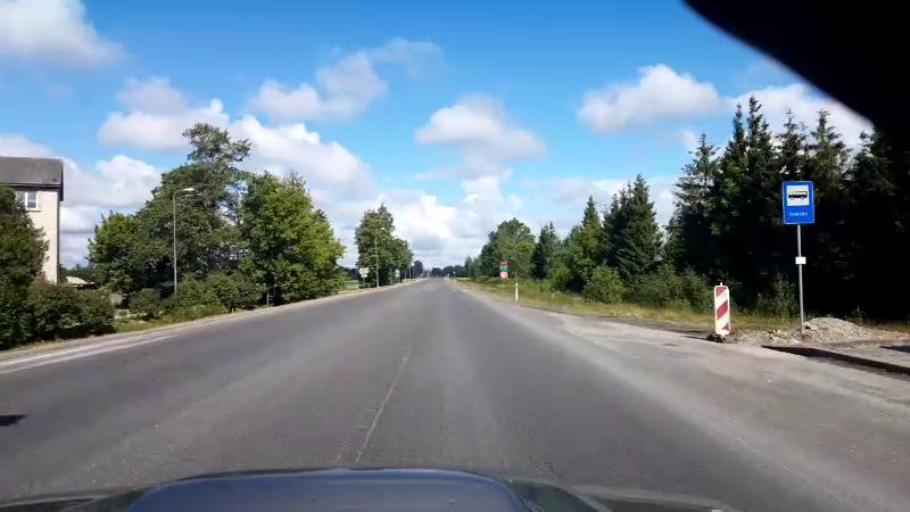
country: LV
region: Bauskas Rajons
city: Bauska
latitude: 56.3985
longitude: 24.2316
